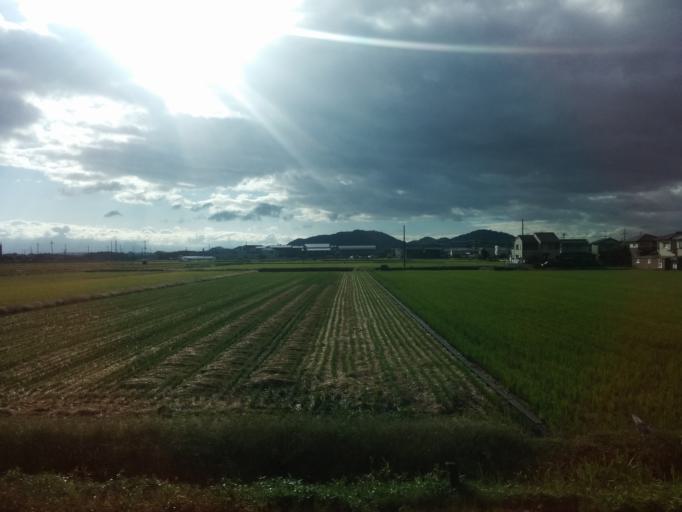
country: JP
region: Shiga Prefecture
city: Omihachiman
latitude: 35.1298
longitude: 136.1117
